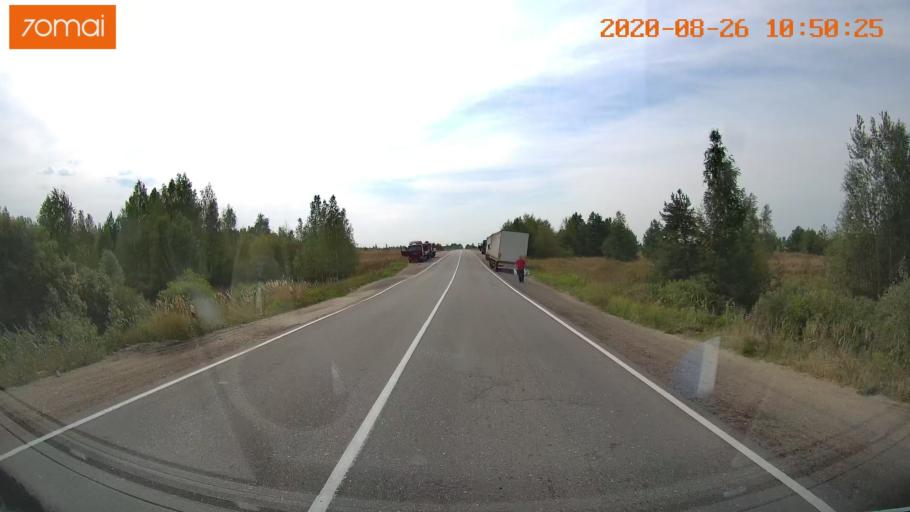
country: RU
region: Rjazan
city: Lashma
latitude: 54.6879
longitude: 41.1569
